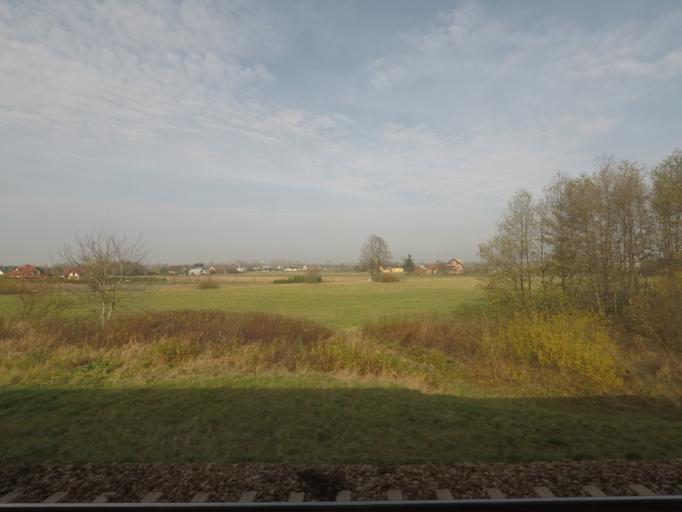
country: PL
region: Subcarpathian Voivodeship
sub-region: Powiat lancucki
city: Gluchow
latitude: 50.0835
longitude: 22.2814
